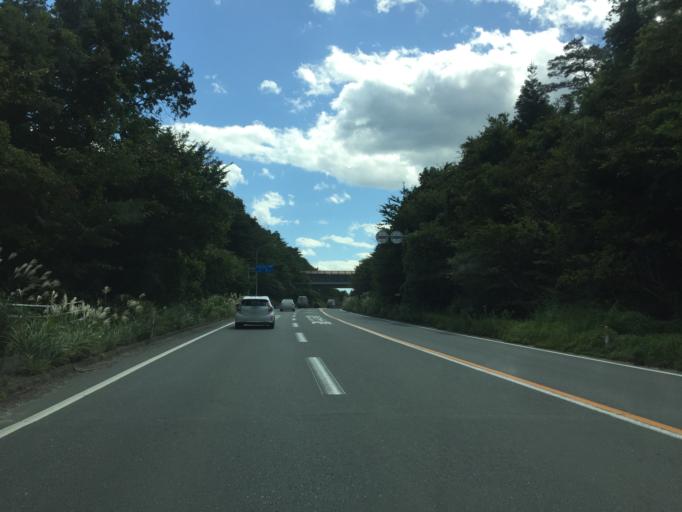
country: JP
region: Fukushima
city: Namie
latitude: 37.4391
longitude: 141.0108
